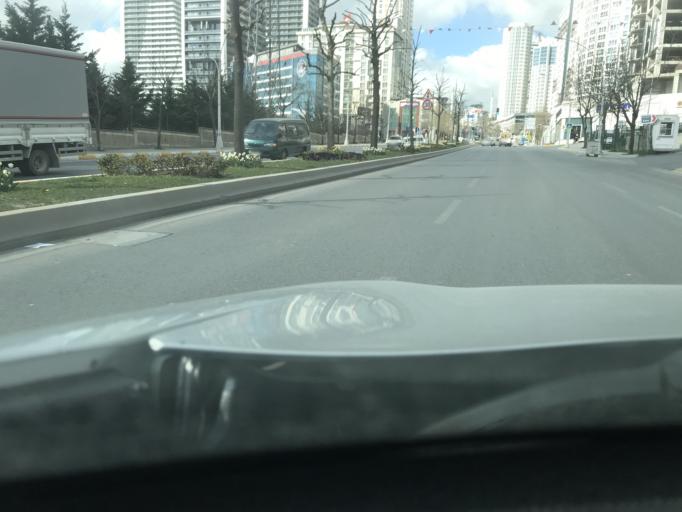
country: TR
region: Istanbul
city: Esenyurt
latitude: 41.0134
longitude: 28.6820
